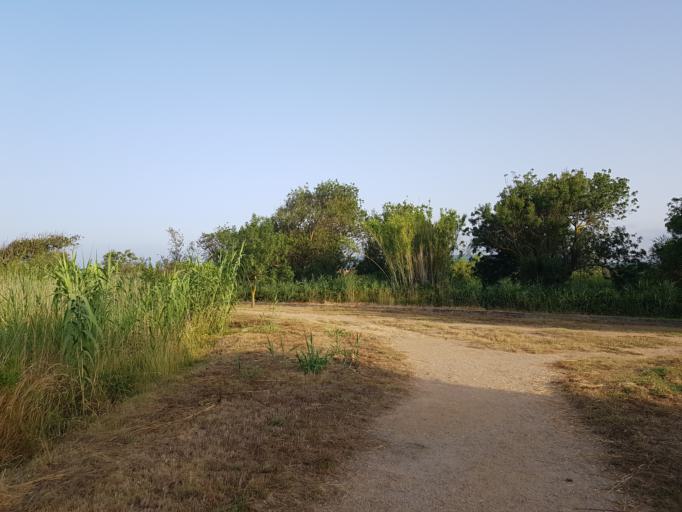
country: ES
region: Catalonia
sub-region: Provincia de Girona
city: Pals
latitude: 42.0067
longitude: 3.1944
